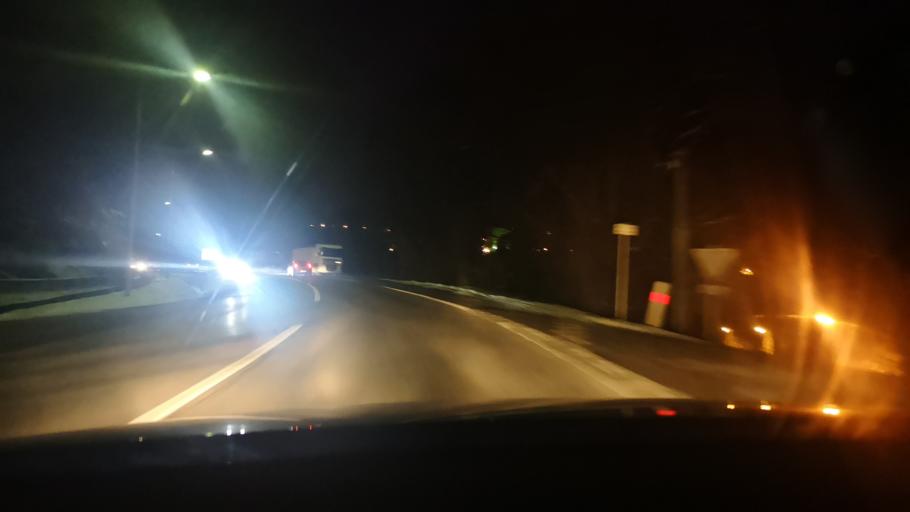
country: FR
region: Rhone-Alpes
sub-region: Departement de la Haute-Savoie
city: Viry
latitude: 46.1211
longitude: 6.0397
